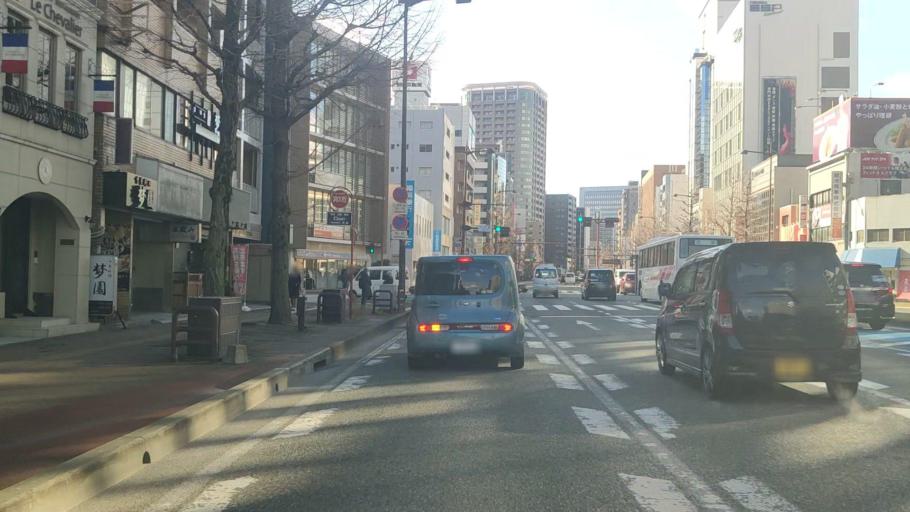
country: JP
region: Fukuoka
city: Fukuoka-shi
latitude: 33.5902
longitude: 130.3907
